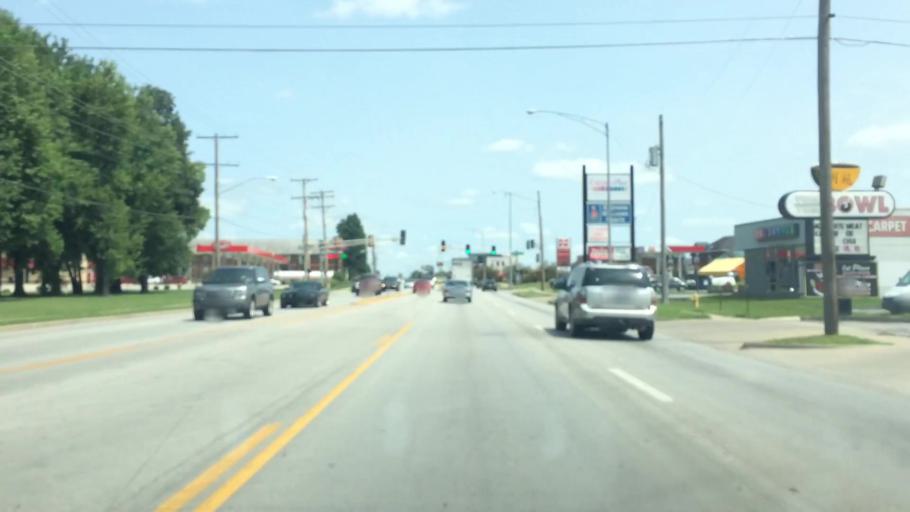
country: US
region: Missouri
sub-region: Greene County
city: Springfield
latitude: 37.1598
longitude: -93.2867
